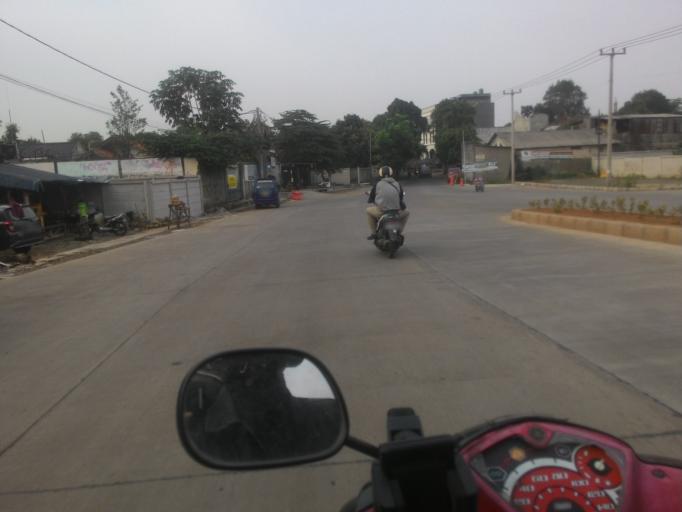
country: ID
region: West Java
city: Depok
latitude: -6.3684
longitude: 106.8133
